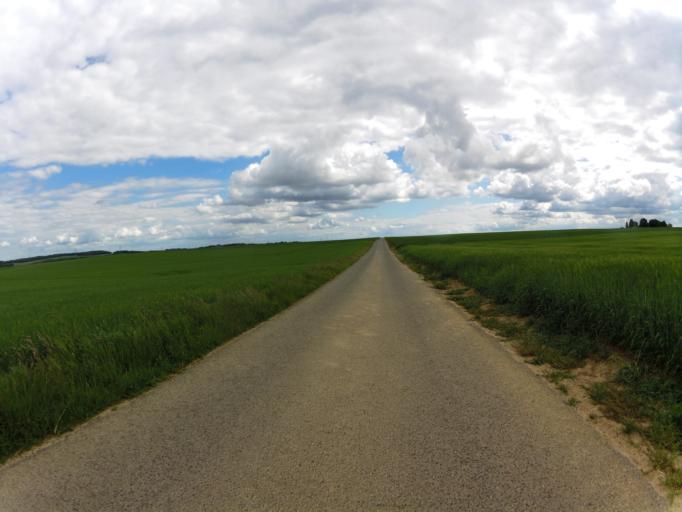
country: DE
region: Bavaria
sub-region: Regierungsbezirk Unterfranken
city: Gaukonigshofen
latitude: 49.6533
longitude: 10.0043
